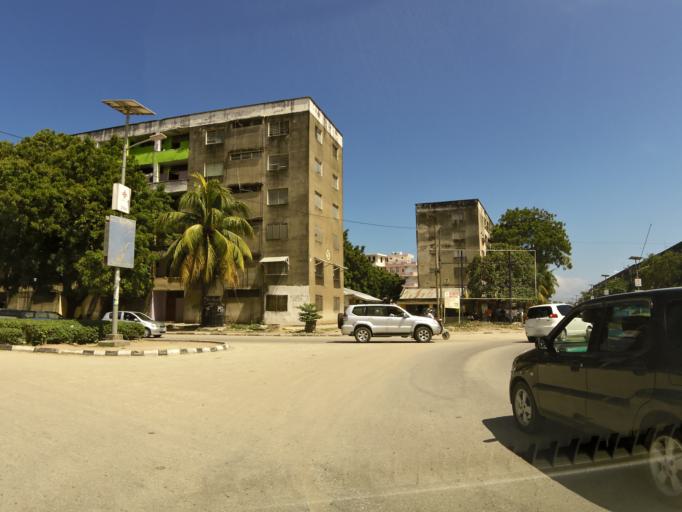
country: TZ
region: Zanzibar Urban/West
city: Zanzibar
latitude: -6.1653
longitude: 39.1990
